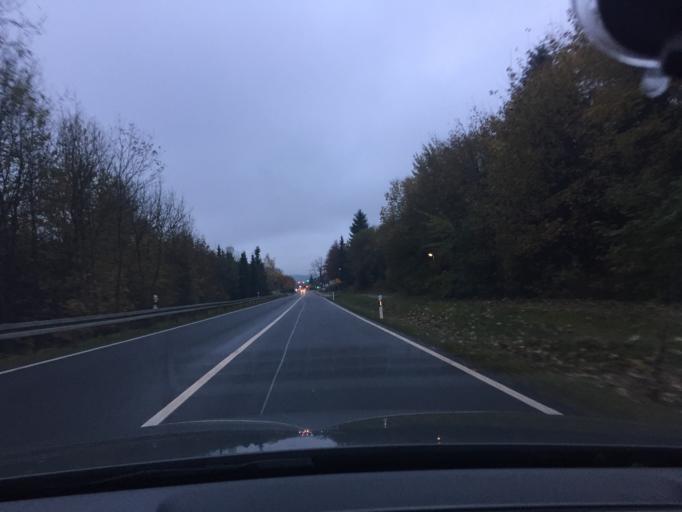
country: DE
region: Saxony
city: Altenberg
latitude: 50.7671
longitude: 13.7479
